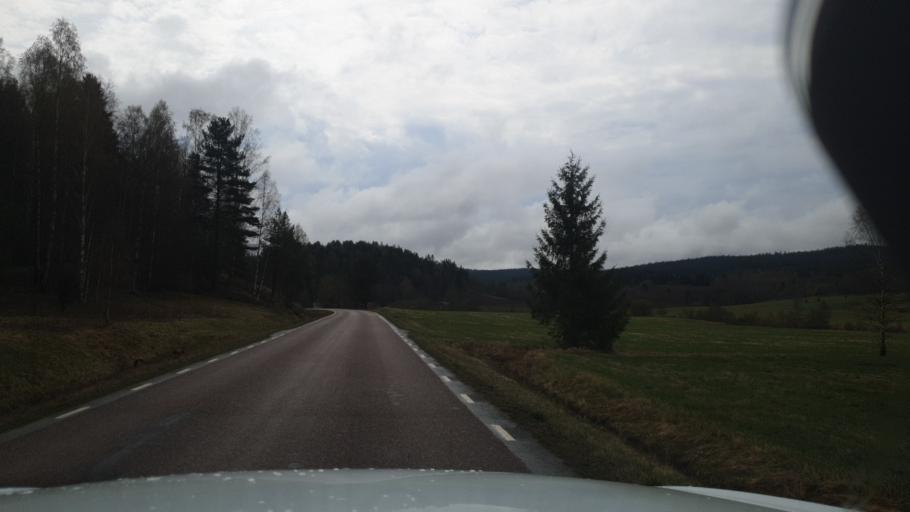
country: NO
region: Ostfold
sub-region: Romskog
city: Romskog
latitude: 59.7042
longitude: 12.0762
